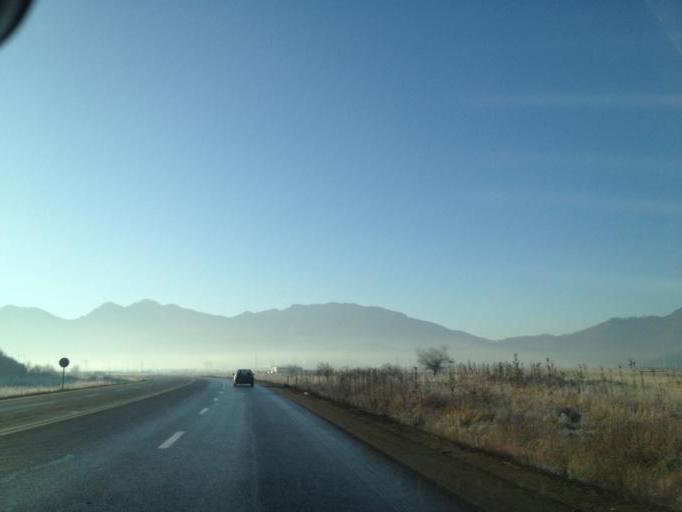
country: RO
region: Brasov
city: Brasov
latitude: 45.6459
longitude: 25.6548
